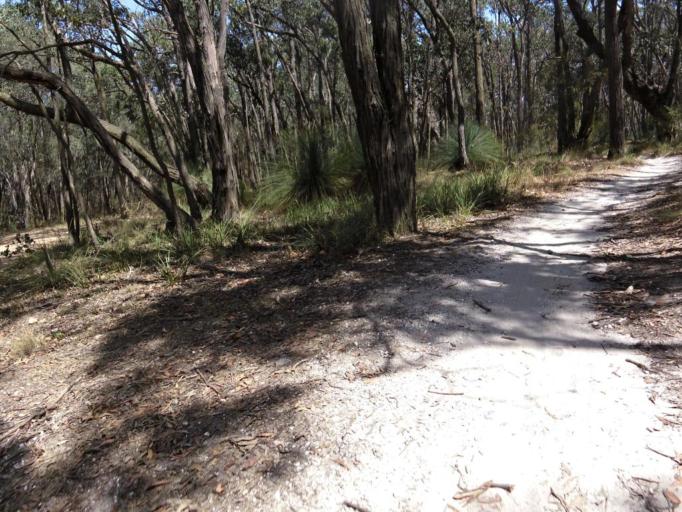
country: AU
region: Victoria
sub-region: Melton
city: Melton West
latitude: -37.5132
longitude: 144.5560
